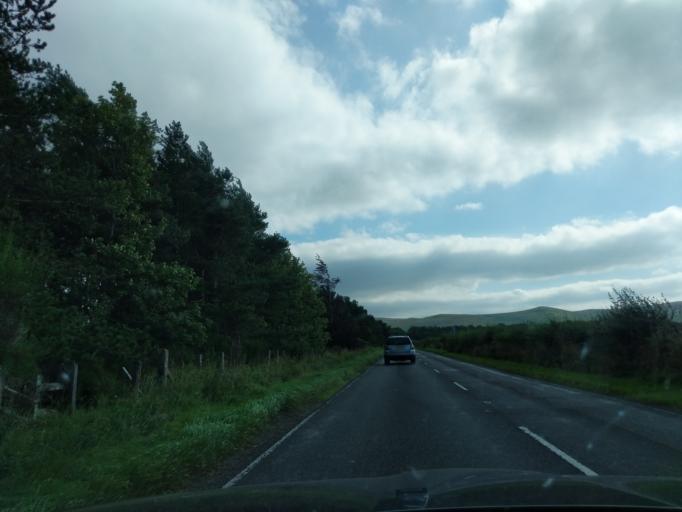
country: GB
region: England
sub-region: Northumberland
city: Ford
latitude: 55.5872
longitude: -2.0932
